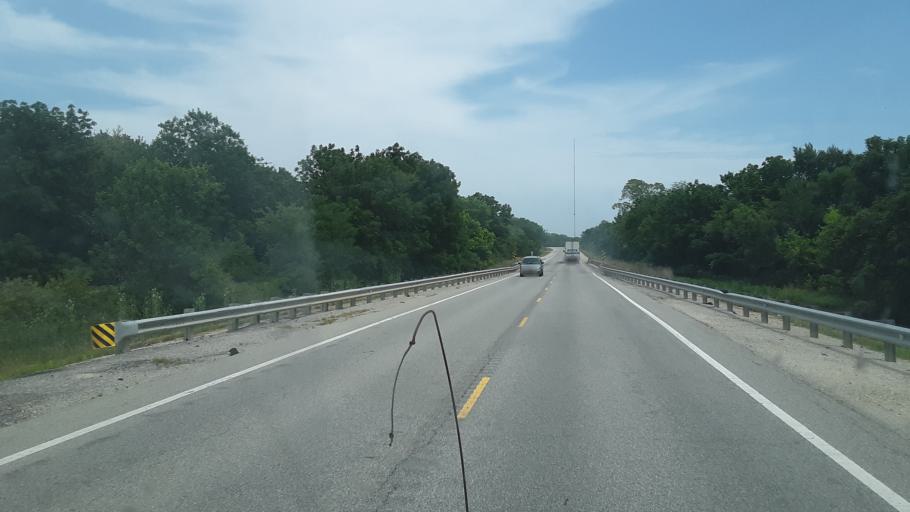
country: US
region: Kansas
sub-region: Allen County
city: Iola
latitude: 37.9132
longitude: -95.1354
